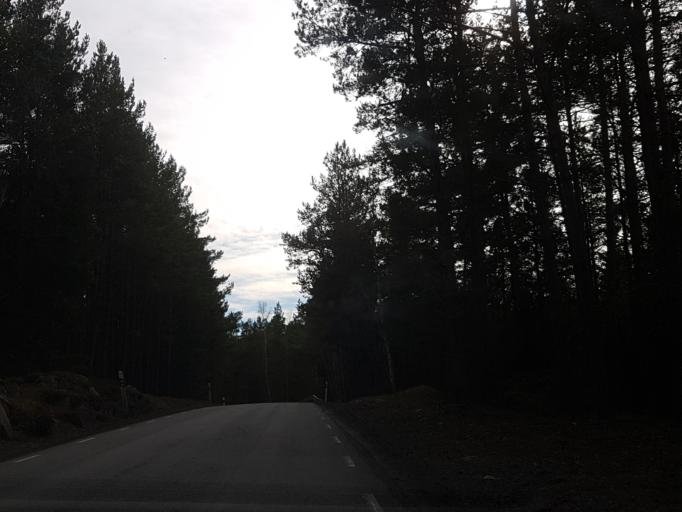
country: SE
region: Stockholm
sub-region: Norrtalje Kommun
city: Norrtalje
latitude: 59.6805
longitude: 18.8358
